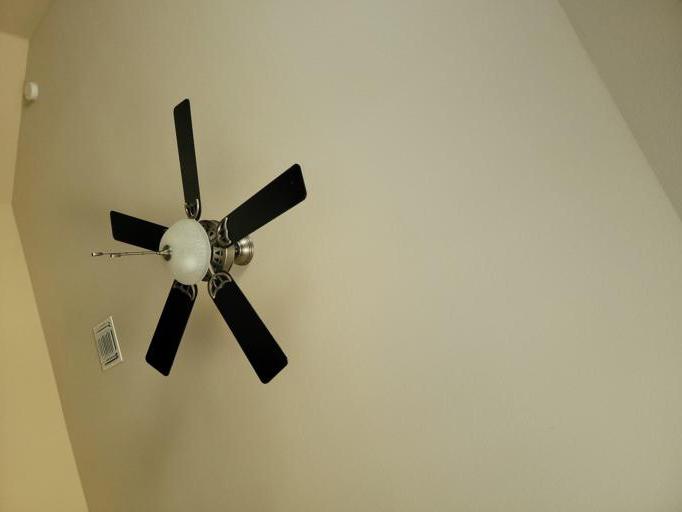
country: US
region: Texas
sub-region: Travis County
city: Manor
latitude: 30.3091
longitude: -97.5316
